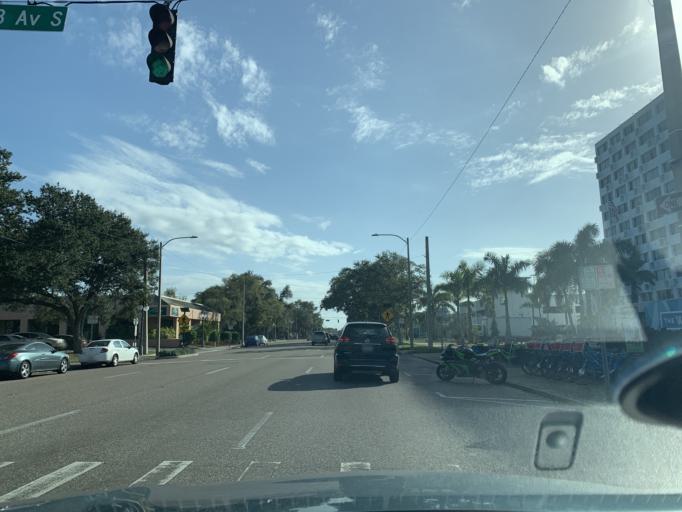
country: US
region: Florida
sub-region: Pinellas County
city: Saint Petersburg
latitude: 27.7685
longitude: -82.6467
